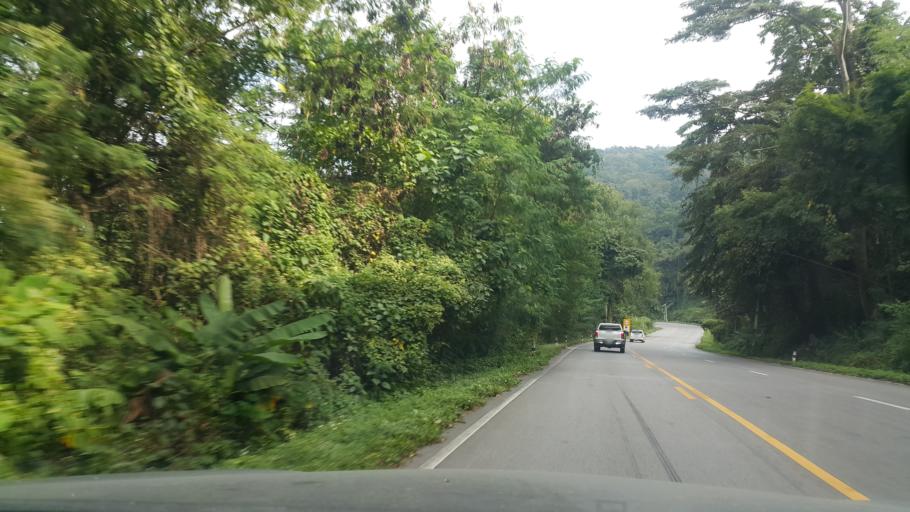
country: TH
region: Phayao
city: Phayao
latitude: 19.0608
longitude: 99.7963
